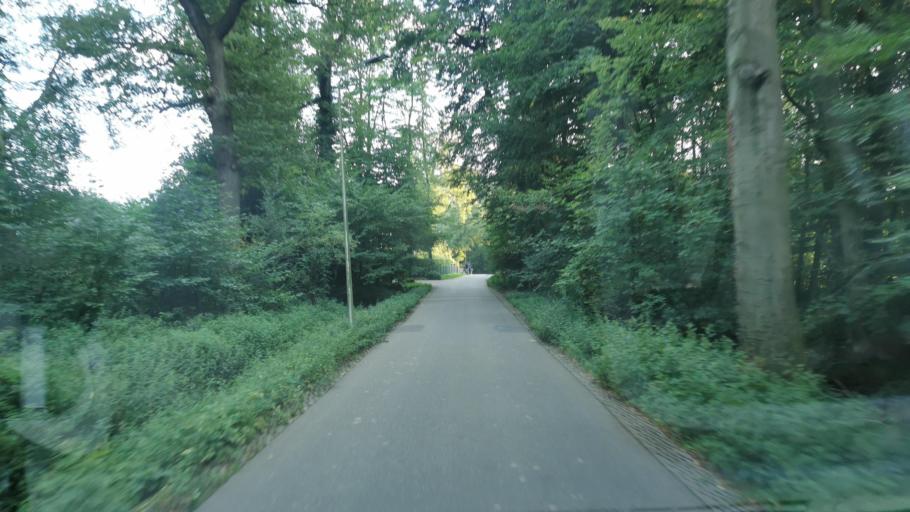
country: NL
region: Overijssel
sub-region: Gemeente Oldenzaal
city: Oldenzaal
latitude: 52.3160
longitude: 6.9463
